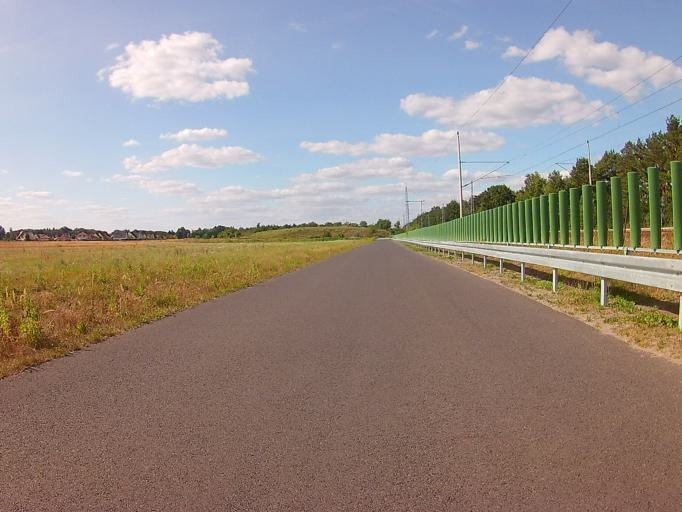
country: DE
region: Brandenburg
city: Zeuthen
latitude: 52.3584
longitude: 13.6216
